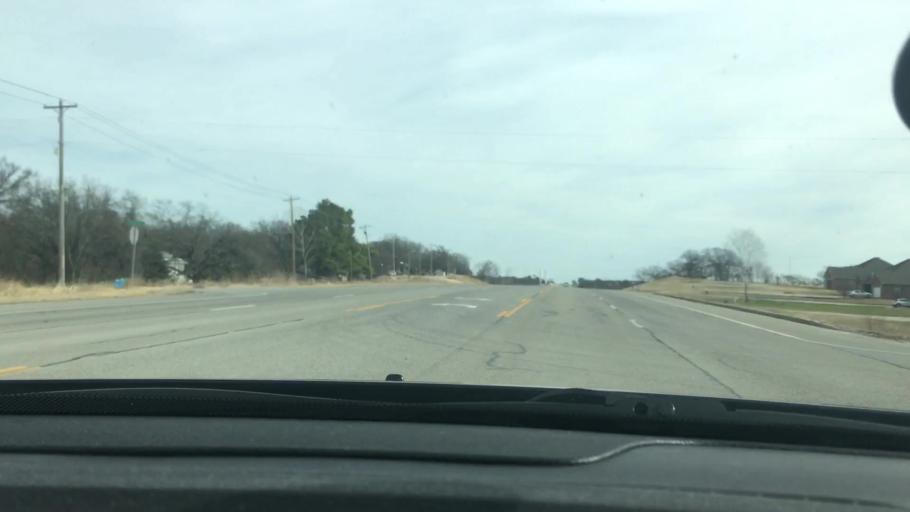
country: US
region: Oklahoma
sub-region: Carter County
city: Dickson
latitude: 34.1871
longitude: -97.0214
